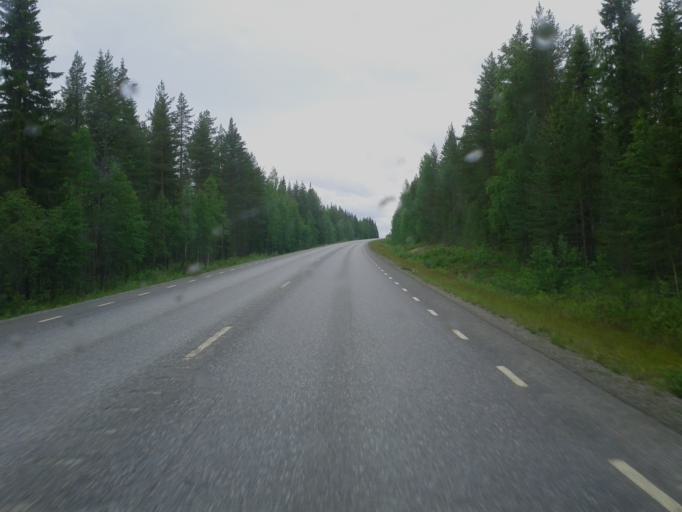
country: SE
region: Vaesterbotten
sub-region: Skelleftea Kommun
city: Langsele
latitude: 64.8969
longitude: 20.1530
